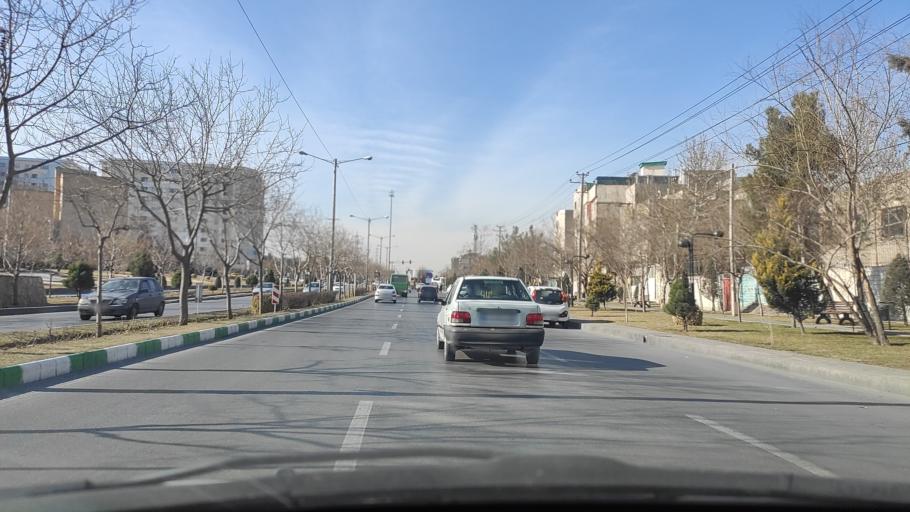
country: IR
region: Razavi Khorasan
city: Mashhad
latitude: 36.2998
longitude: 59.5123
